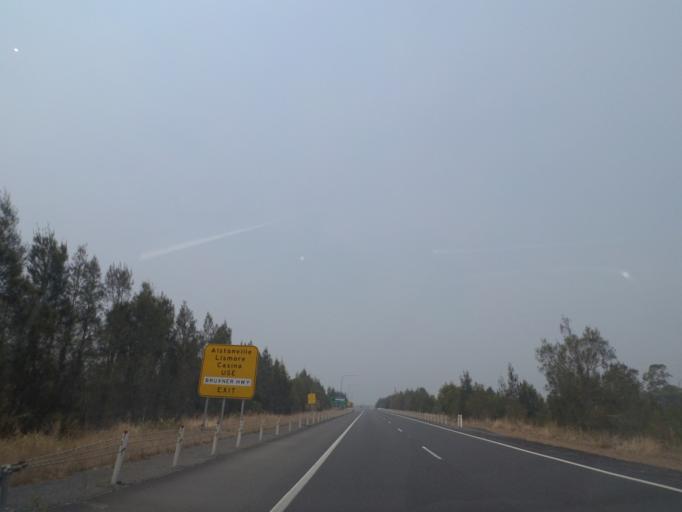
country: AU
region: New South Wales
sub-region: Ballina
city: Ballina
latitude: -28.8643
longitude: 153.5090
